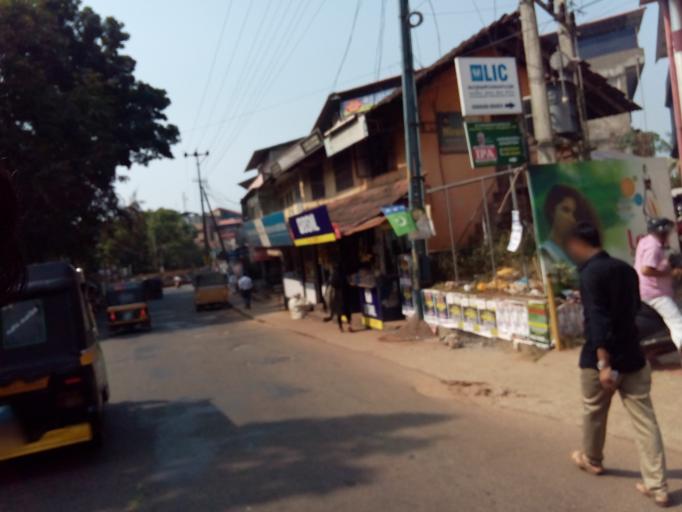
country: IN
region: Kerala
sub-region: Kozhikode
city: Badagara
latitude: 11.6004
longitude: 75.5899
